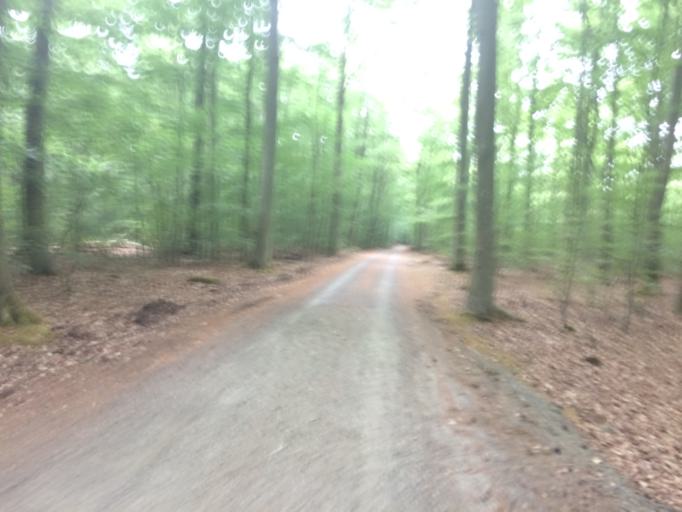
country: DK
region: Capital Region
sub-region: Bornholm Kommune
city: Ronne
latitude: 55.1340
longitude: 14.7158
